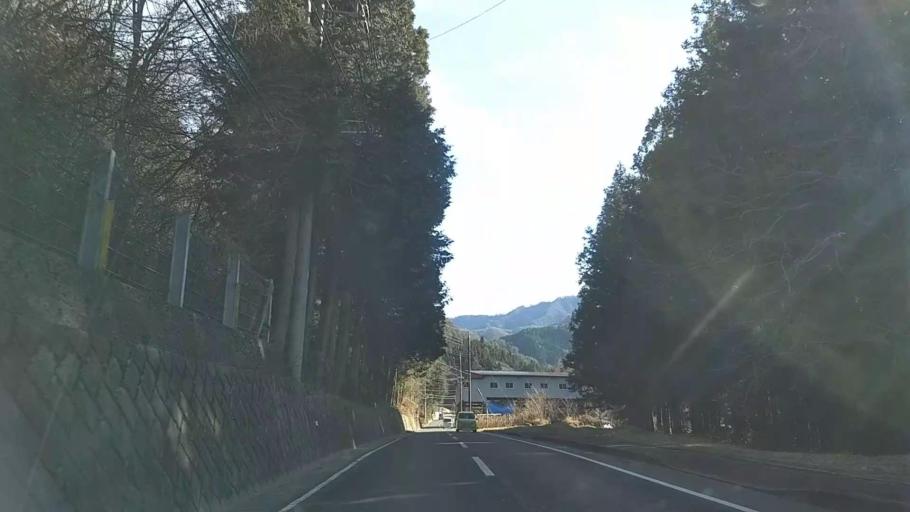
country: JP
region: Yamanashi
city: Otsuki
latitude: 35.5259
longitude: 138.9236
